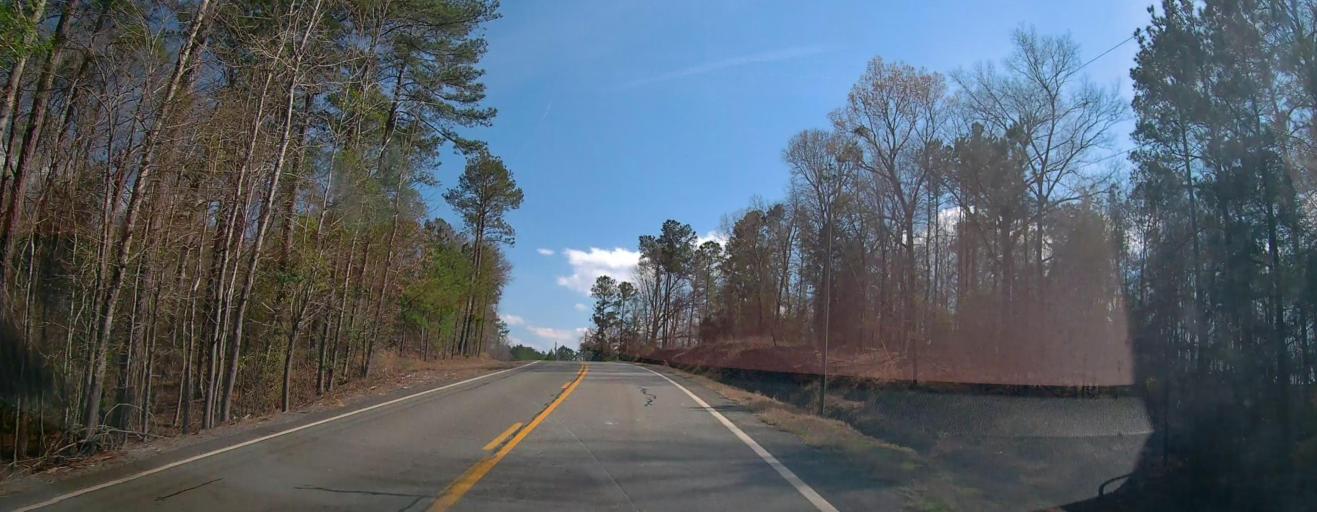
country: US
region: Georgia
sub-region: Wilkinson County
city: Gordon
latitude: 32.8248
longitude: -83.3272
